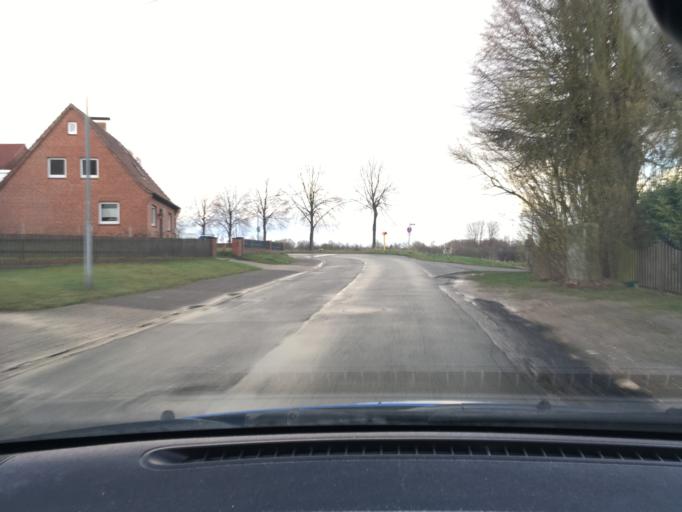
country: DE
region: Lower Saxony
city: Harmstorf
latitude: 53.3776
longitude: 9.9909
